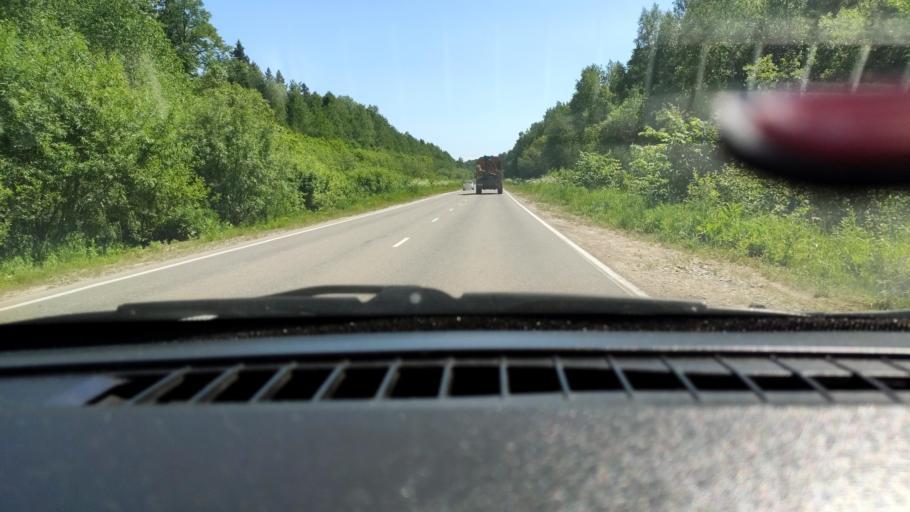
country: RU
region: Perm
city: Novyye Lyady
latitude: 58.0240
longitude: 56.6383
